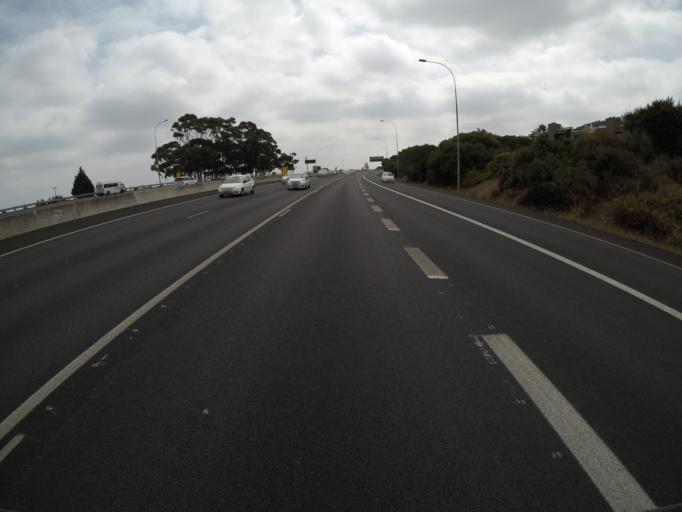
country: ZA
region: Western Cape
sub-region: City of Cape Town
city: Sunset Beach
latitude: -33.8895
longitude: 18.6040
